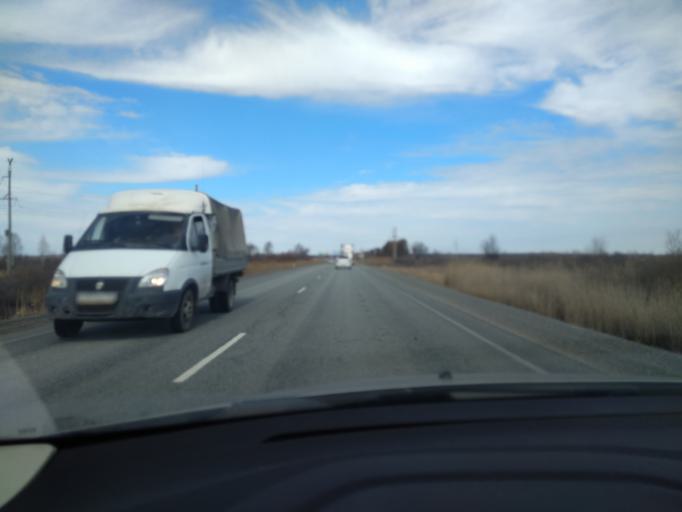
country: RU
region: Sverdlovsk
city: Pyshma
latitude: 57.0262
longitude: 63.4044
